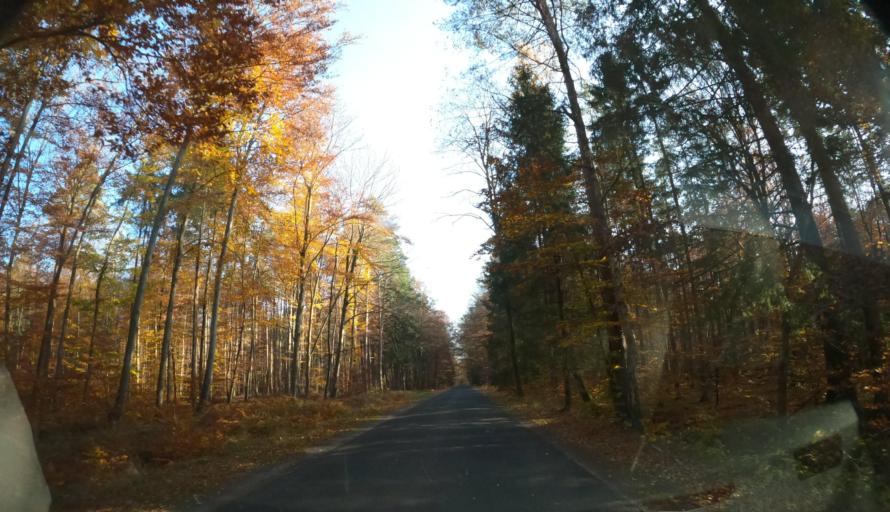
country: PL
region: West Pomeranian Voivodeship
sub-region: Powiat koszalinski
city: Polanow
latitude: 54.2370
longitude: 16.7398
